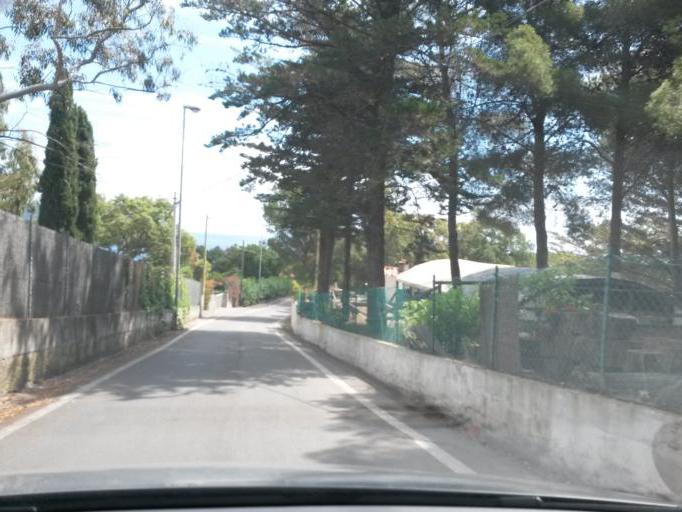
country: IT
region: Tuscany
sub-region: Provincia di Livorno
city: Porto Azzurro
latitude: 42.7562
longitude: 10.3968
